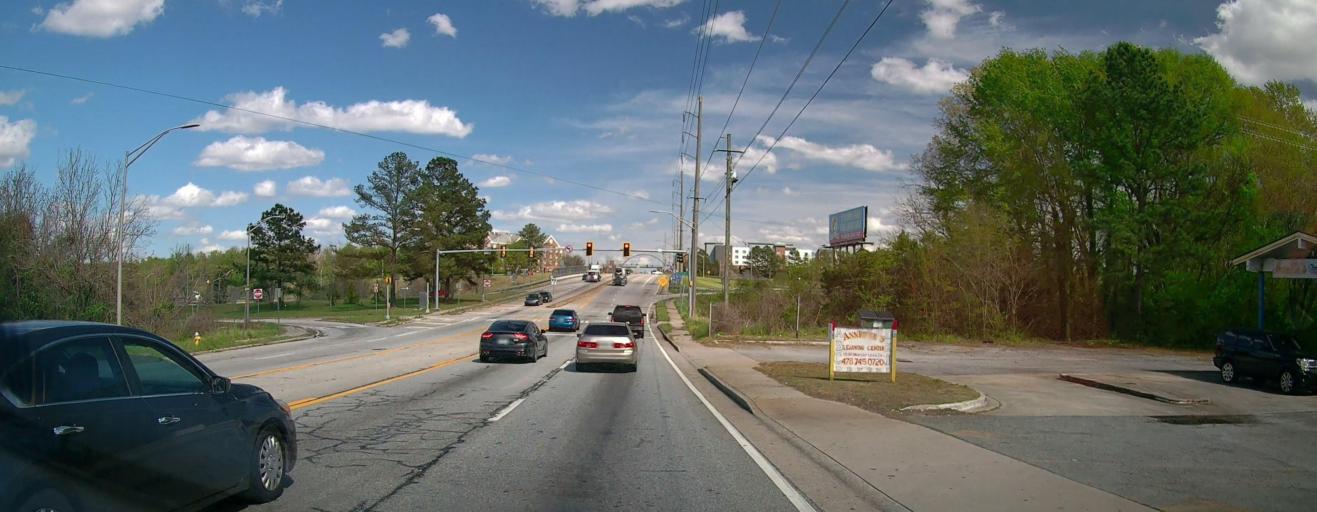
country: US
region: Georgia
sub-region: Bibb County
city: Macon
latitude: 32.8256
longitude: -83.6596
